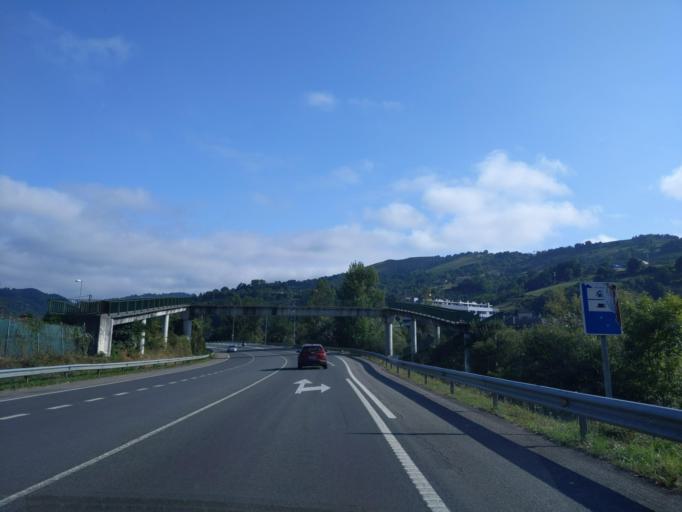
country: ES
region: Asturias
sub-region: Province of Asturias
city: Pola de Laviana
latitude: 43.2467
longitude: -5.5680
